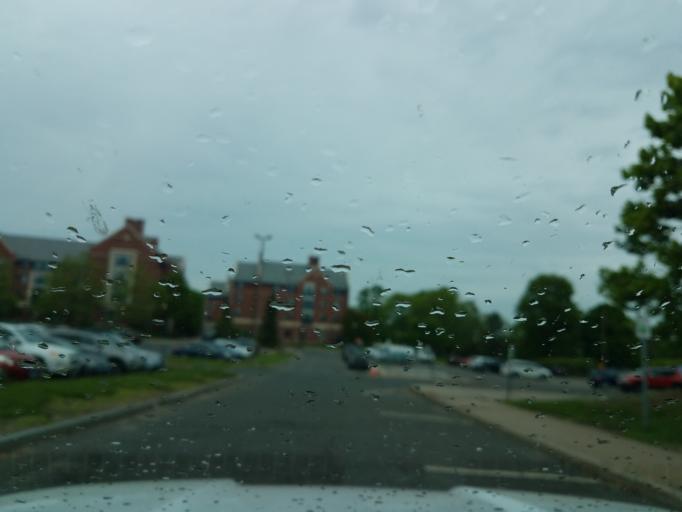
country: US
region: Connecticut
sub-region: Tolland County
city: Storrs
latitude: 41.8037
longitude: -72.2462
